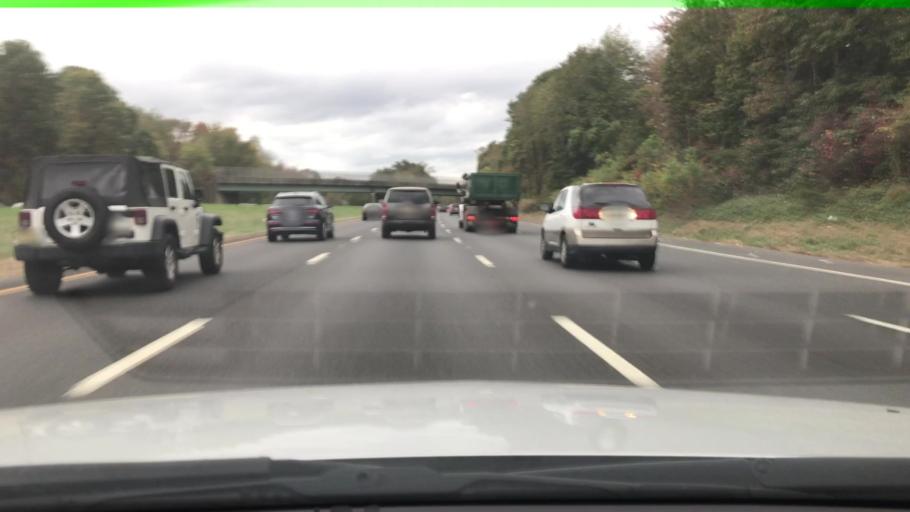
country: US
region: New Jersey
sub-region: Burlington County
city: Roebling
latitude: 40.0806
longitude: -74.7661
